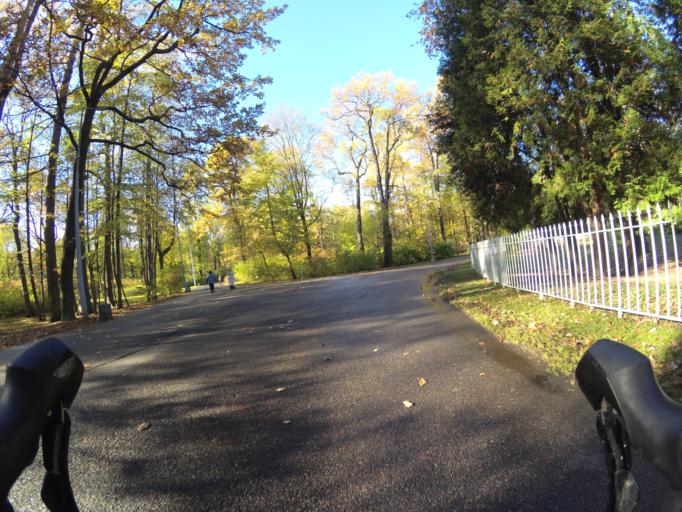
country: RU
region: Leningrad
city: Krestovskiy ostrov
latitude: 59.9776
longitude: 30.2682
